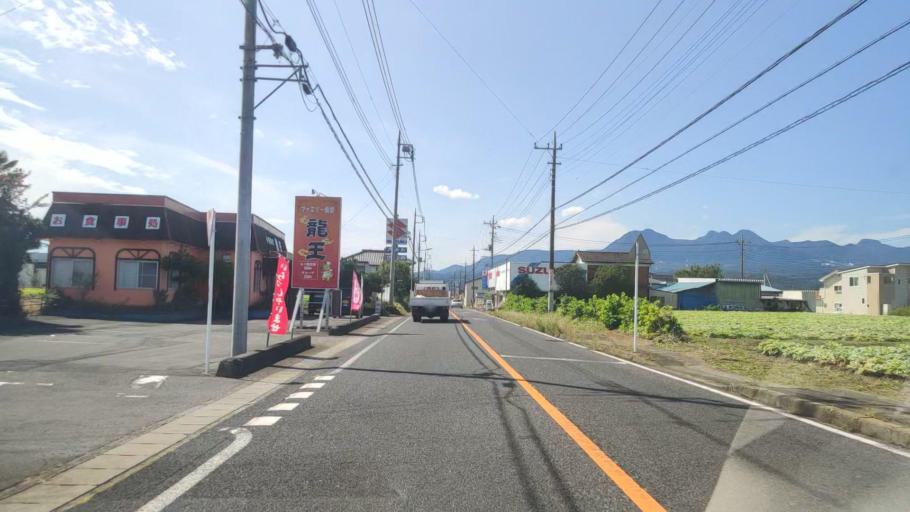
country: JP
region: Gunma
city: Shibukawa
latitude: 36.5316
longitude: 139.0168
